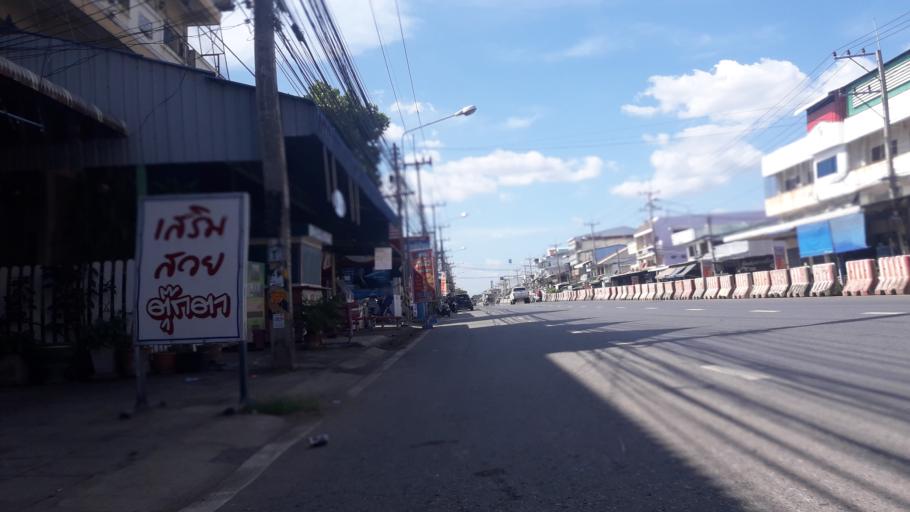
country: TH
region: Phichit
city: Thap Khlo
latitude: 16.1672
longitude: 100.5803
